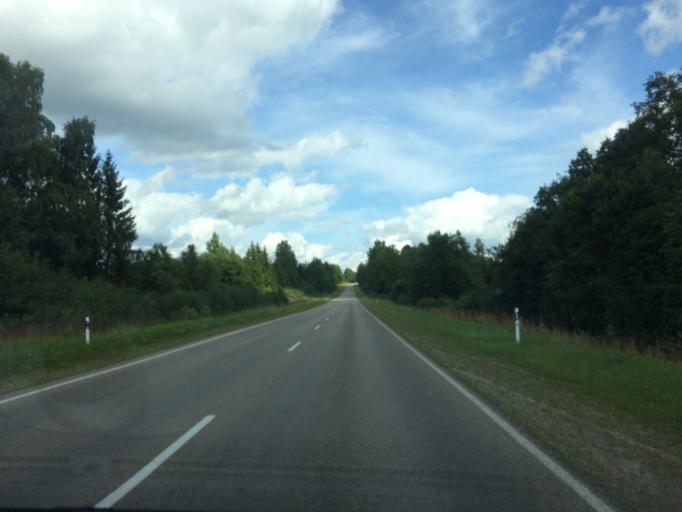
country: LV
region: Rezekne
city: Rezekne
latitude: 56.6227
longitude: 27.4567
